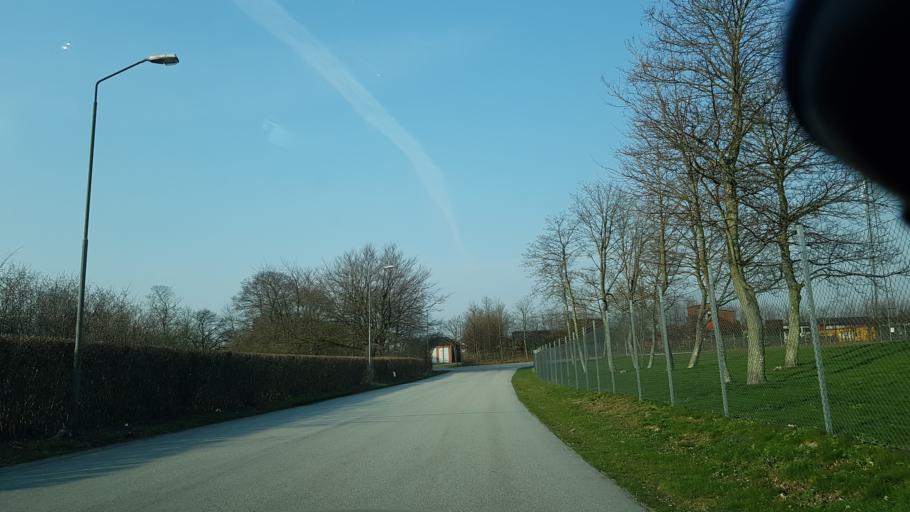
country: SE
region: Skane
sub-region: Ystads Kommun
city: Ystad
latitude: 55.4438
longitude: 13.8418
